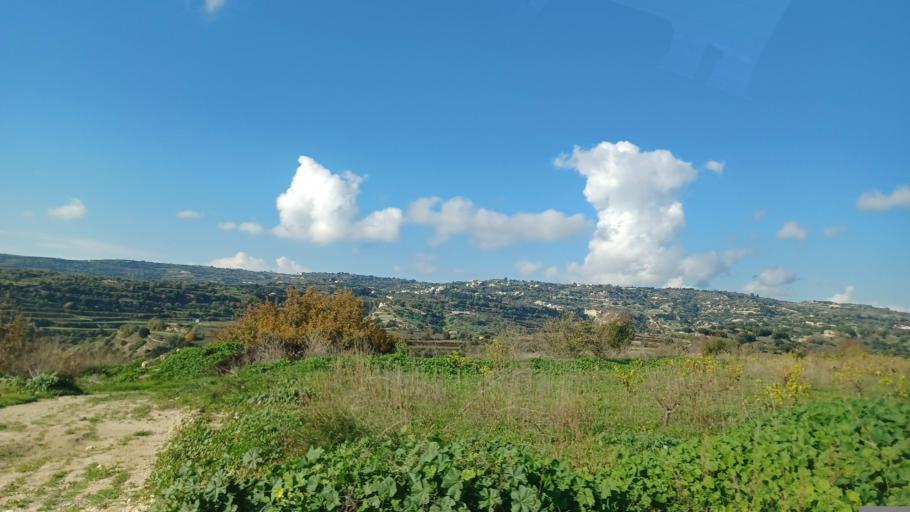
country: CY
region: Pafos
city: Mesogi
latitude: 34.8466
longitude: 32.5228
